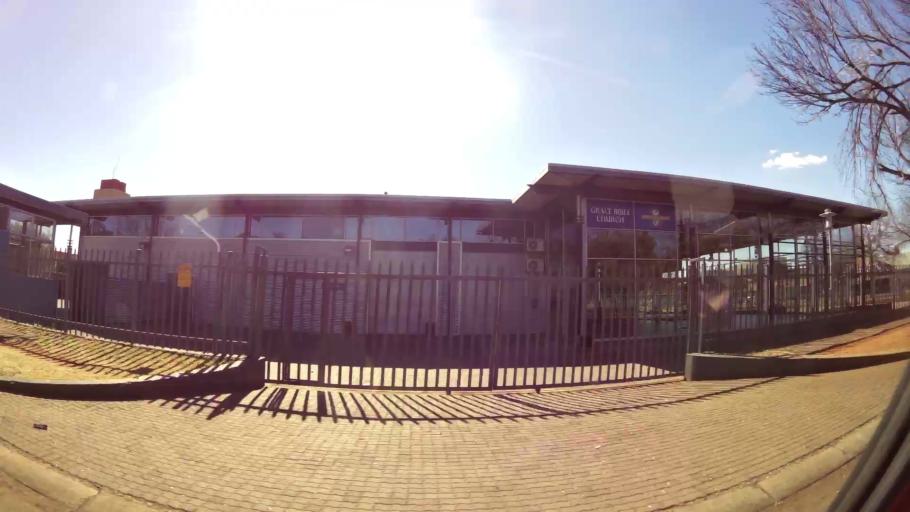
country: ZA
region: Gauteng
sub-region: West Rand District Municipality
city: Carletonville
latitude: -26.3595
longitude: 27.3965
